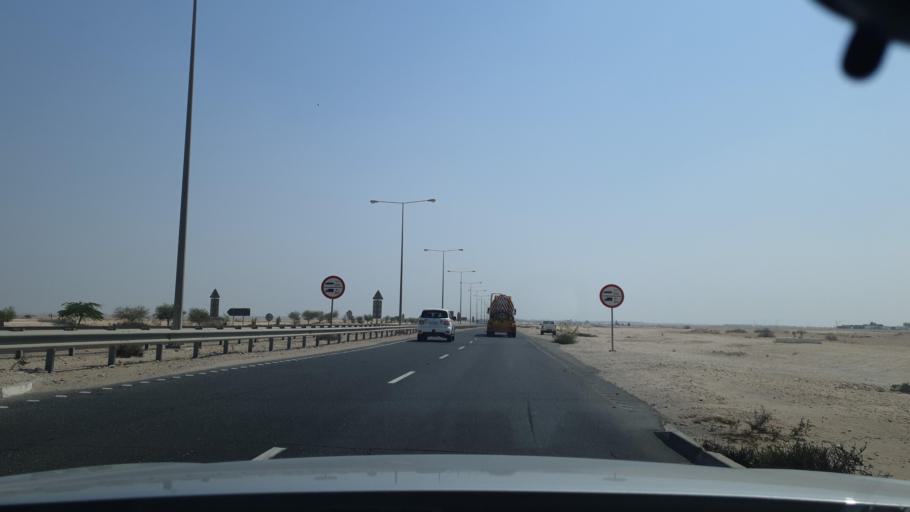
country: QA
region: Al Khawr
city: Al Khawr
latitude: 25.7534
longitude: 51.4761
